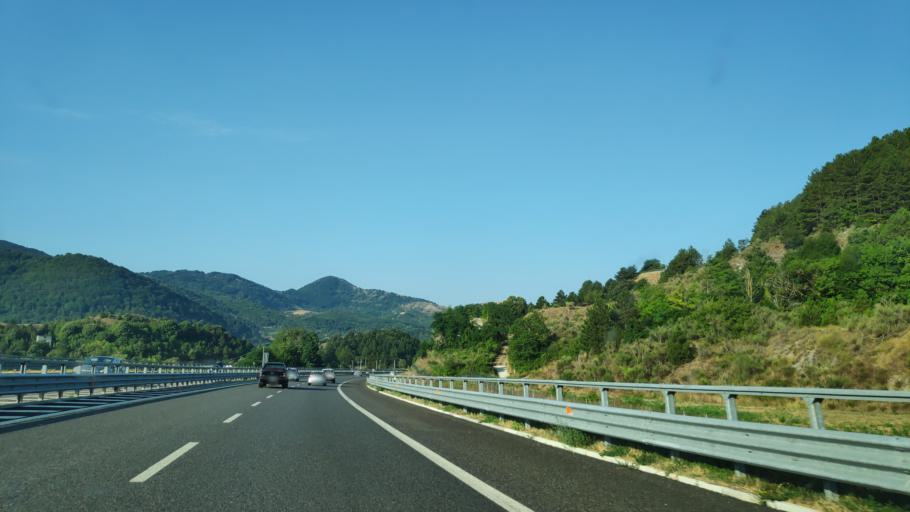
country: IT
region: Calabria
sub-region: Provincia di Cosenza
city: Mormanno
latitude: 39.8810
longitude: 16.0097
